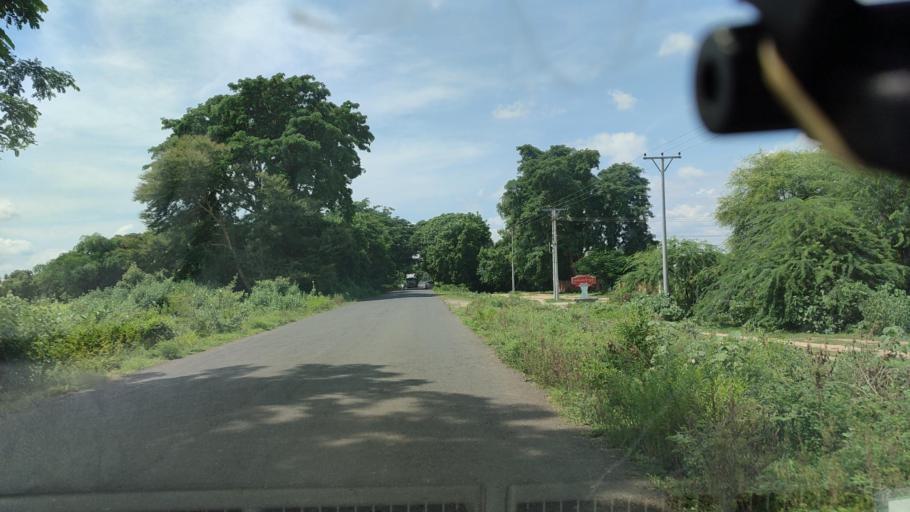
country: MM
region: Magway
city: Pakokku
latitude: 21.2509
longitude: 95.0274
